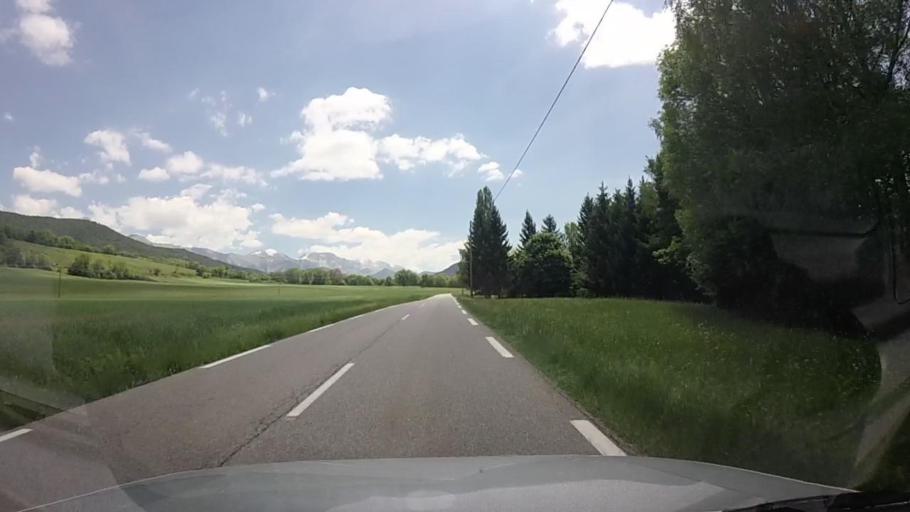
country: FR
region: Provence-Alpes-Cote d'Azur
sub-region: Departement des Alpes-de-Haute-Provence
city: Seyne-les-Alpes
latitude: 44.3619
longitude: 6.3285
